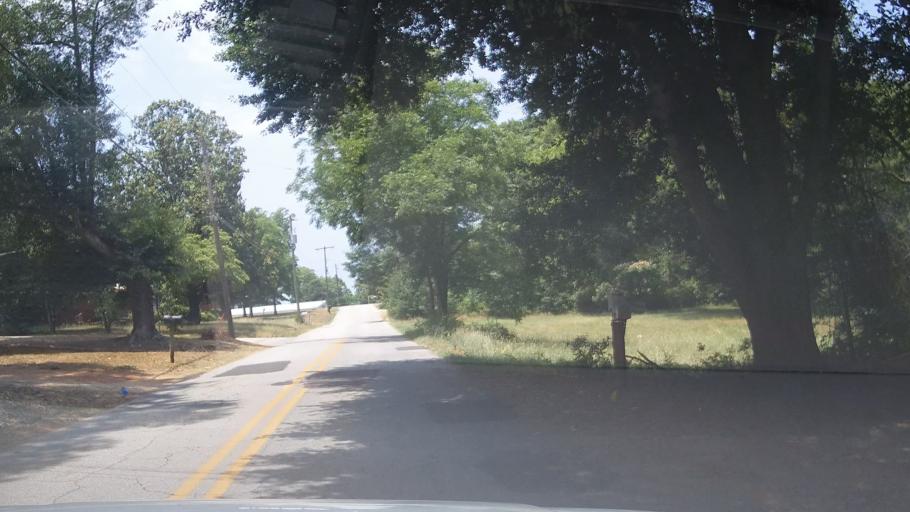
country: US
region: Georgia
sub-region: Hart County
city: Hartwell
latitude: 34.3449
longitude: -82.9353
